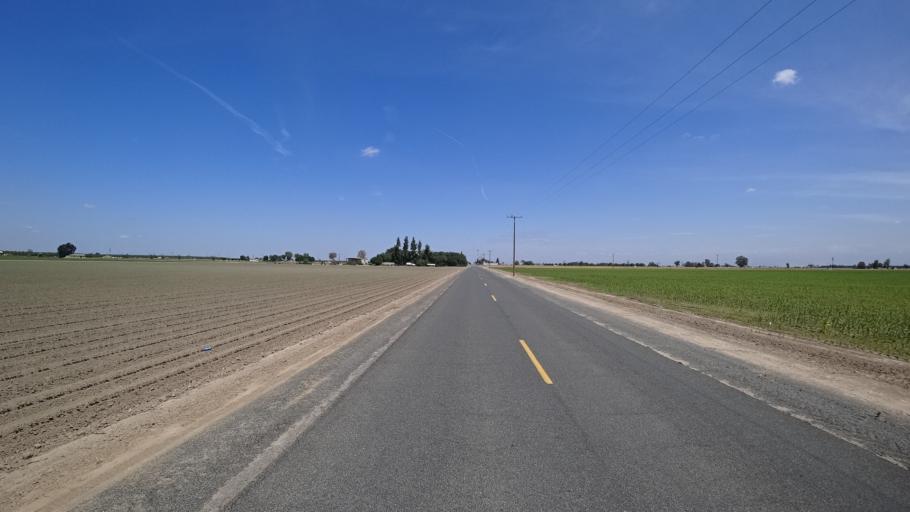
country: US
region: California
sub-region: Tulare County
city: Goshen
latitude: 36.3217
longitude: -119.4754
